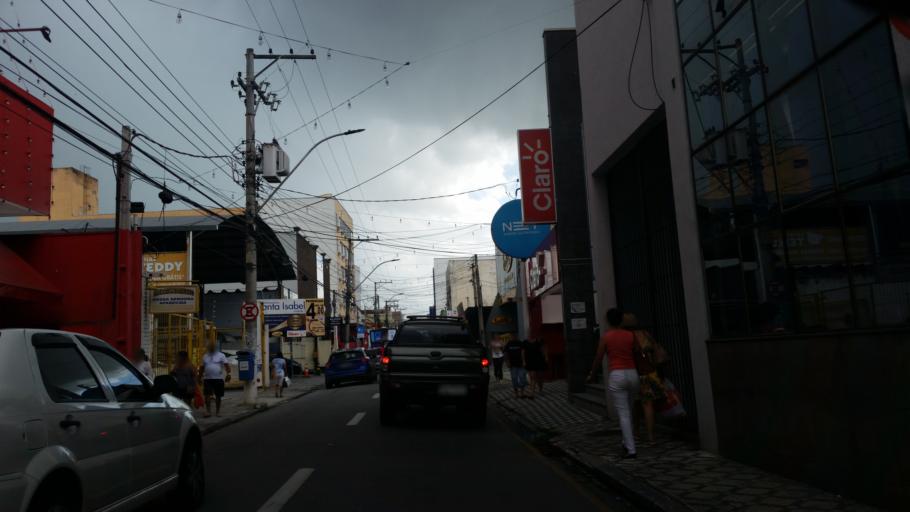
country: BR
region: Sao Paulo
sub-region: Taubate
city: Taubate
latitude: -23.0272
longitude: -45.5555
